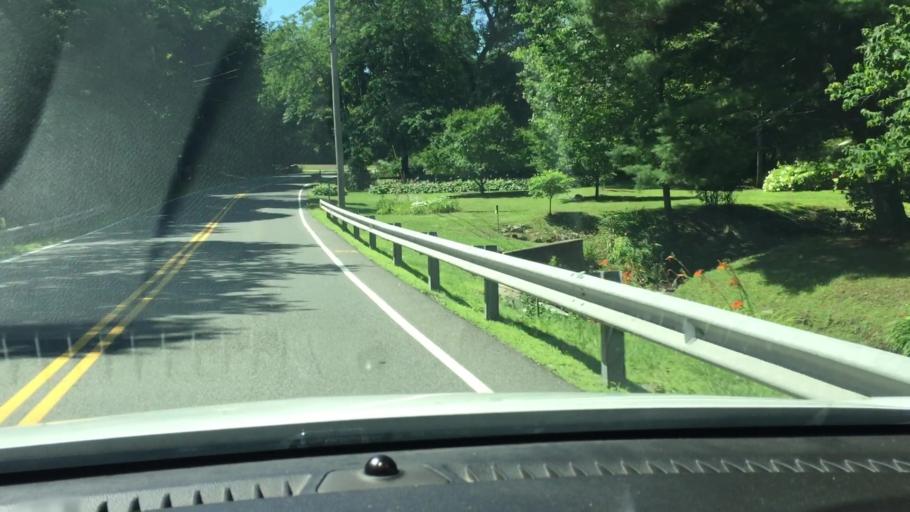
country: US
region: Massachusetts
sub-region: Berkshire County
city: Lenox
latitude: 42.3811
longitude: -73.2566
